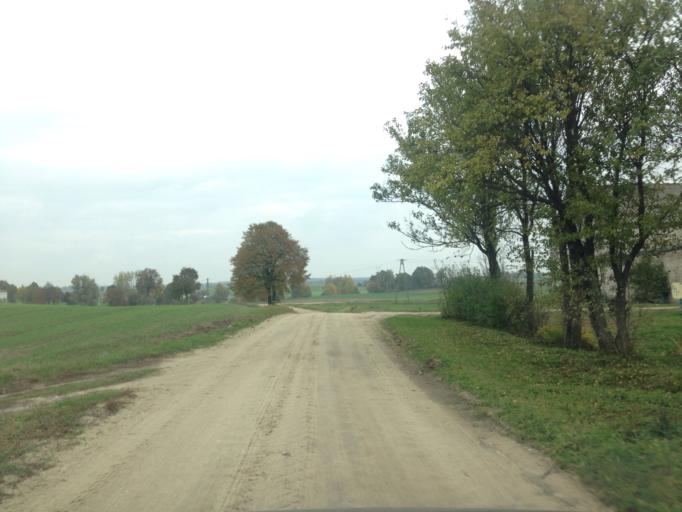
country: PL
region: Kujawsko-Pomorskie
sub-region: Powiat brodnicki
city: Brzozie
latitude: 53.3099
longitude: 19.6931
